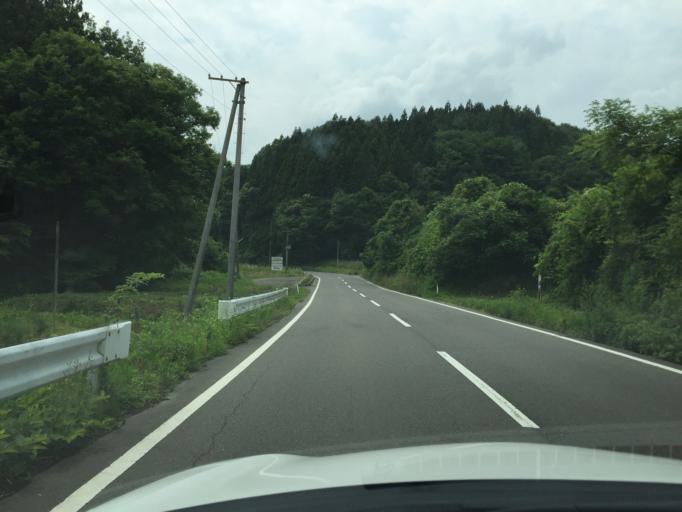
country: JP
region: Fukushima
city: Ishikawa
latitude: 37.2050
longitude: 140.4694
